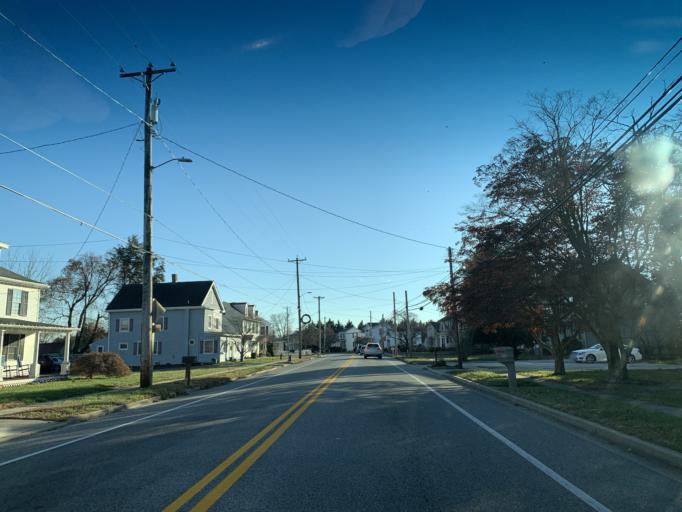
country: US
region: Delaware
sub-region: New Castle County
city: Middletown
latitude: 39.3442
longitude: -75.8793
